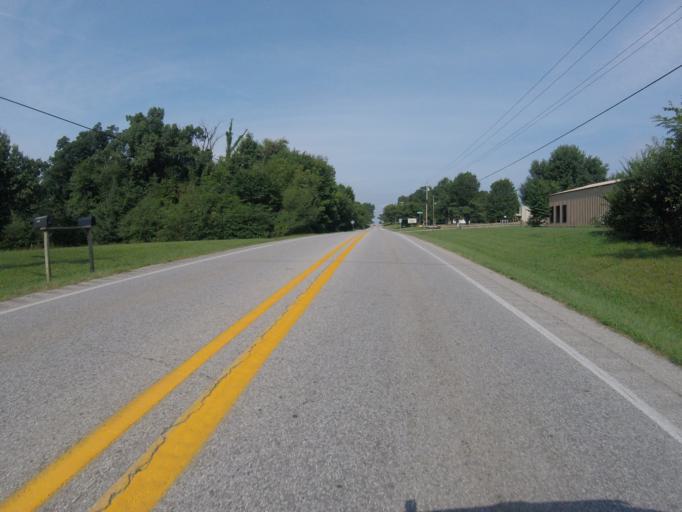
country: US
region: Arkansas
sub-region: Washington County
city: Farmington
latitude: 36.0758
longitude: -94.2682
